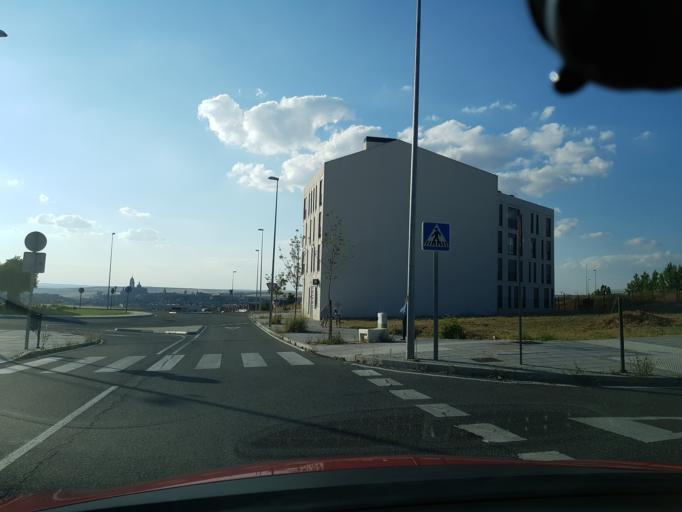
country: ES
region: Castille and Leon
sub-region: Provincia de Segovia
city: Segovia
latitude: 40.9372
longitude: -4.1046
